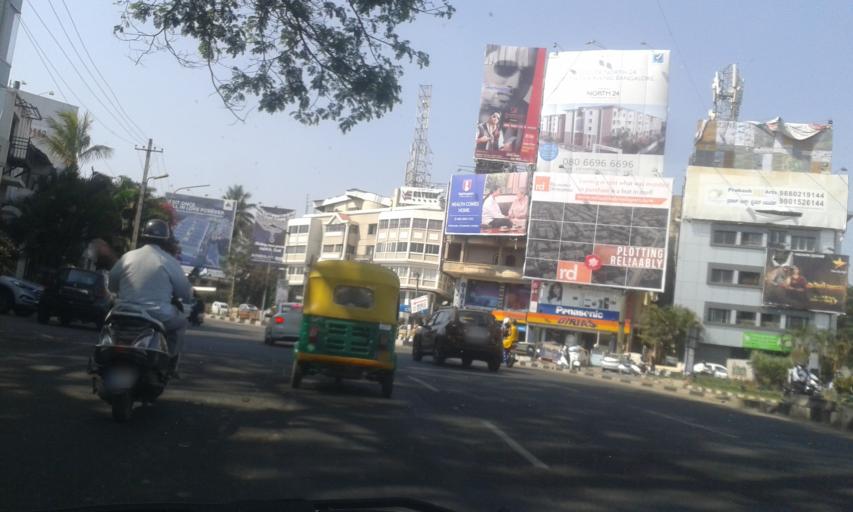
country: IN
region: Karnataka
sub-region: Bangalore Urban
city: Bangalore
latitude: 13.0030
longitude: 77.5840
